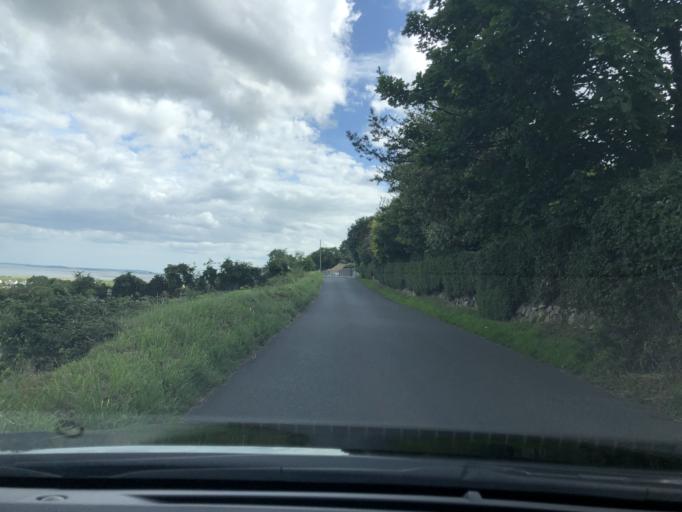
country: GB
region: Northern Ireland
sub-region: Ards District
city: Newtownards
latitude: 54.5820
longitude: -5.7115
